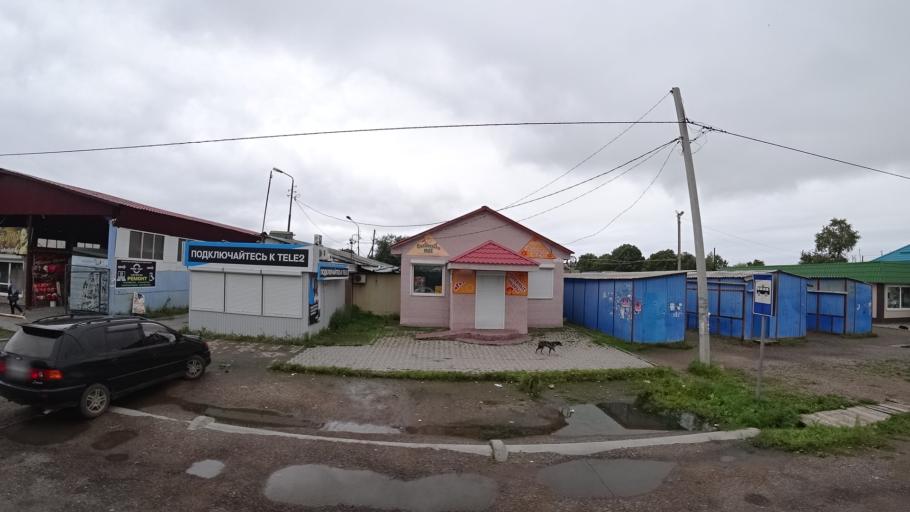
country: RU
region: Primorskiy
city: Chernigovka
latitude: 44.3442
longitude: 132.5735
